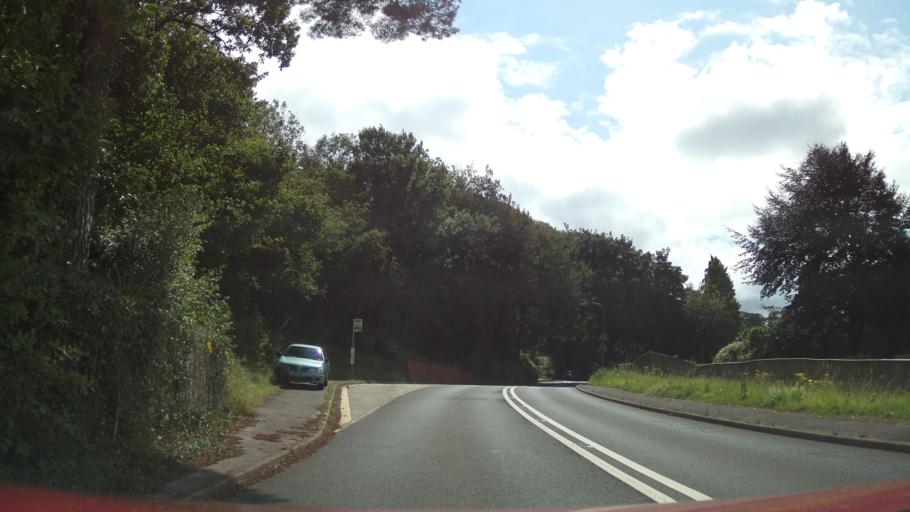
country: GB
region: England
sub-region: Borough of Torbay
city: Torquay
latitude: 50.5052
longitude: -3.5255
